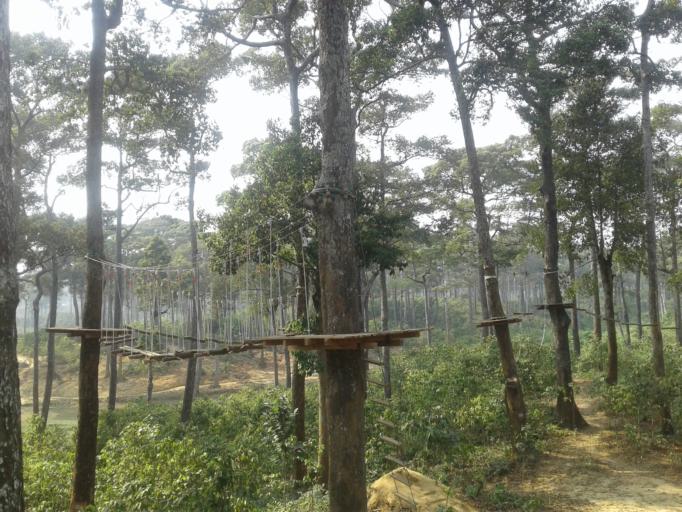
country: BD
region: Chittagong
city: Cox's Bazar
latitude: 21.6277
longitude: 92.0771
